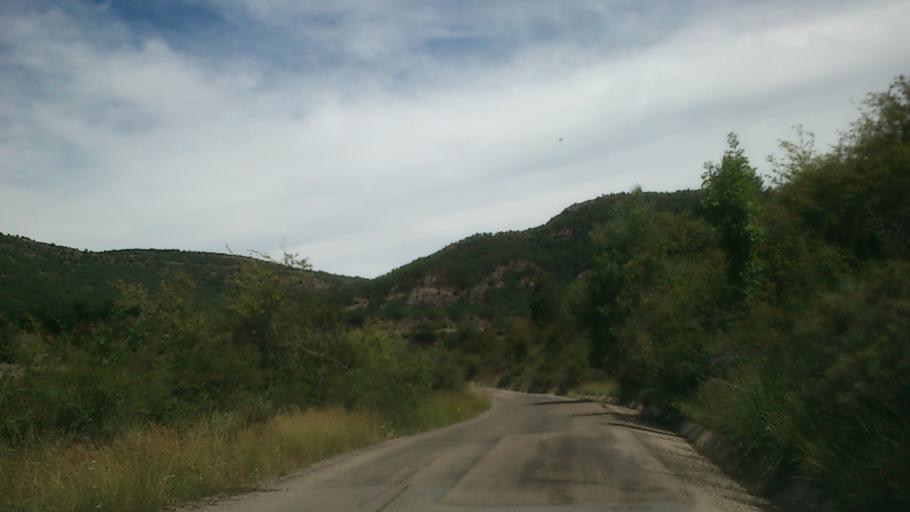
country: ES
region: Aragon
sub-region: Provincia de Huesca
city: Arguis
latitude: 42.3159
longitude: -0.3170
